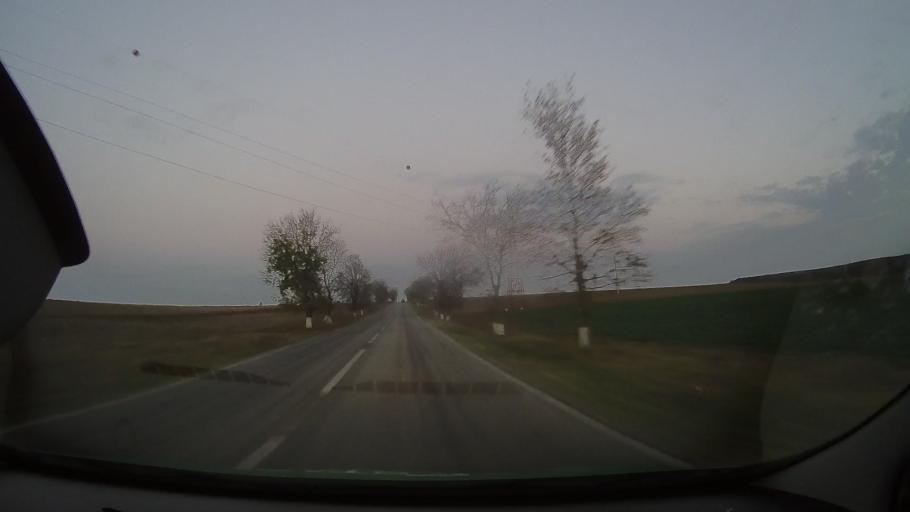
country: RO
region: Constanta
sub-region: Comuna Baneasa
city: Baneasa
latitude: 44.0688
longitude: 27.7208
